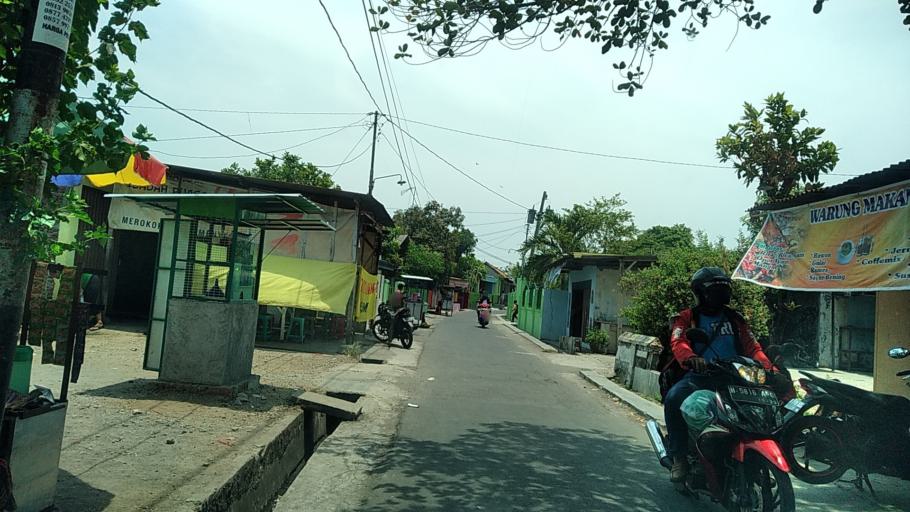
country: ID
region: Central Java
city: Semarang
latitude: -7.0091
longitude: 110.4506
